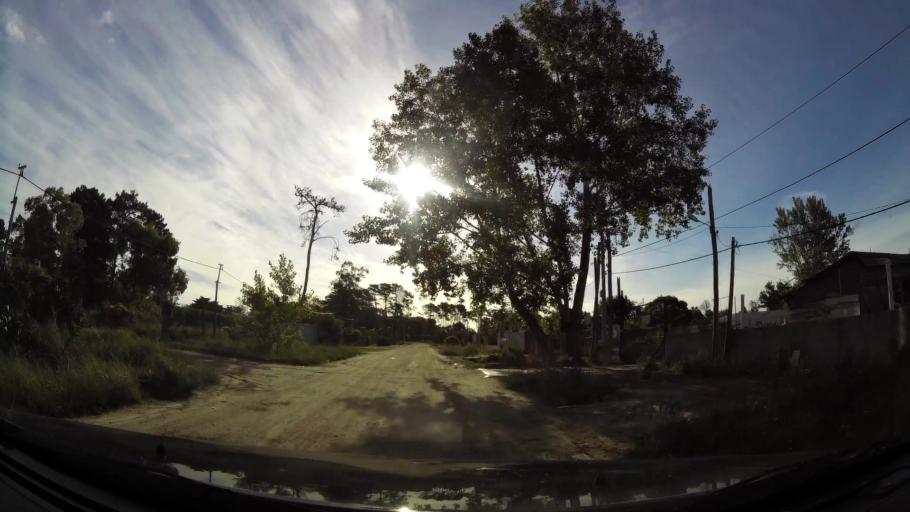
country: UY
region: Canelones
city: Empalme Olmos
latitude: -34.7790
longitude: -55.8570
